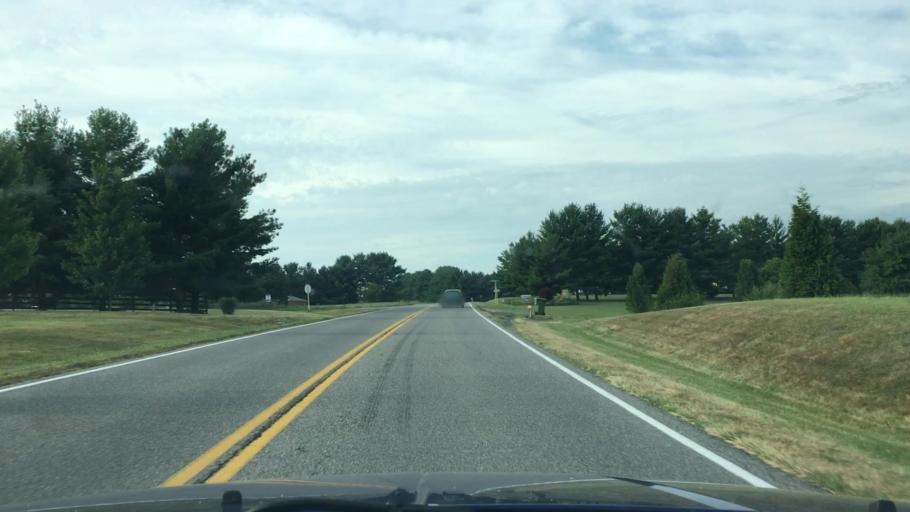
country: US
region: Virginia
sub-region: City of Waynesboro
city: Waynesboro
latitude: 38.1073
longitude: -78.9025
